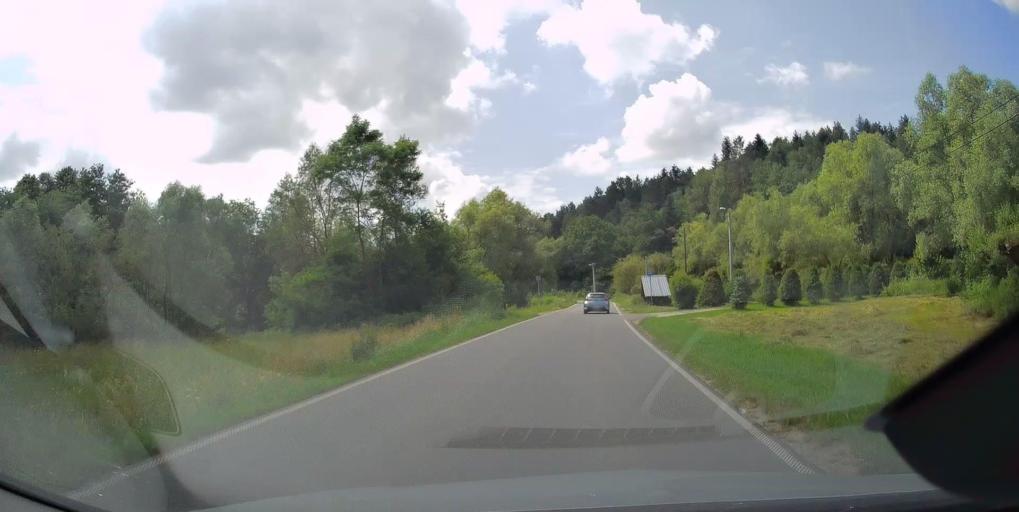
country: PL
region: Lesser Poland Voivodeship
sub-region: Powiat nowosadecki
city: Korzenna
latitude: 49.7432
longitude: 20.7687
